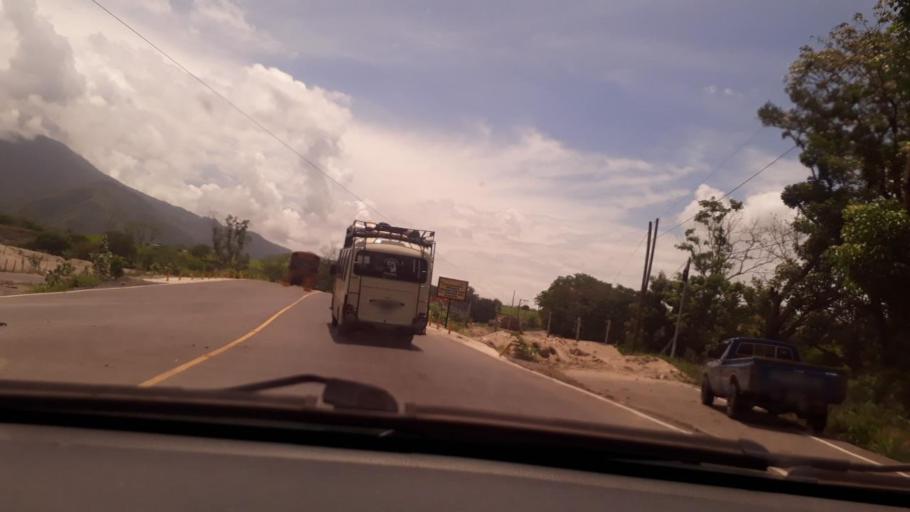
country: GT
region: Zacapa
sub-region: Municipio de Zacapa
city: Gualan
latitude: 15.0926
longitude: -89.4384
